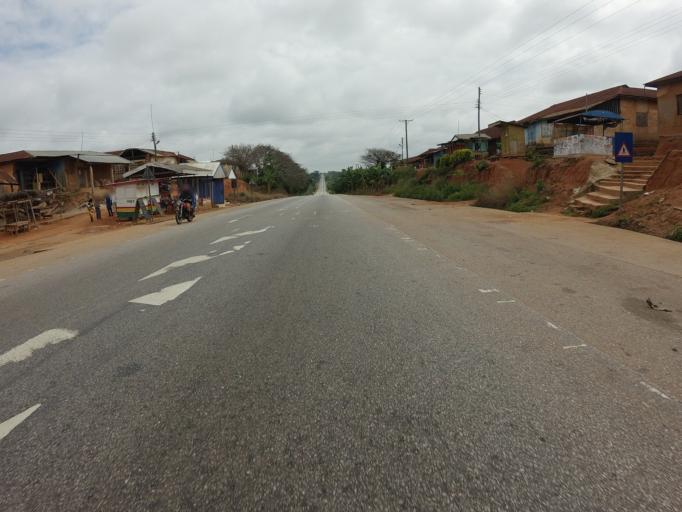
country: GH
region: Ashanti
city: Mampong
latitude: 7.0524
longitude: -1.7106
